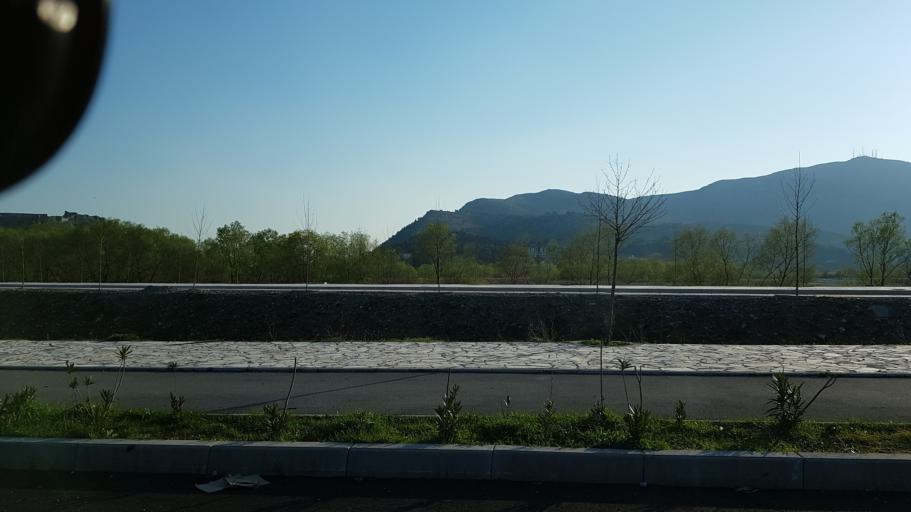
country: AL
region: Shkoder
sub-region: Rrethi i Shkodres
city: Shkoder
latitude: 42.0602
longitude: 19.4964
